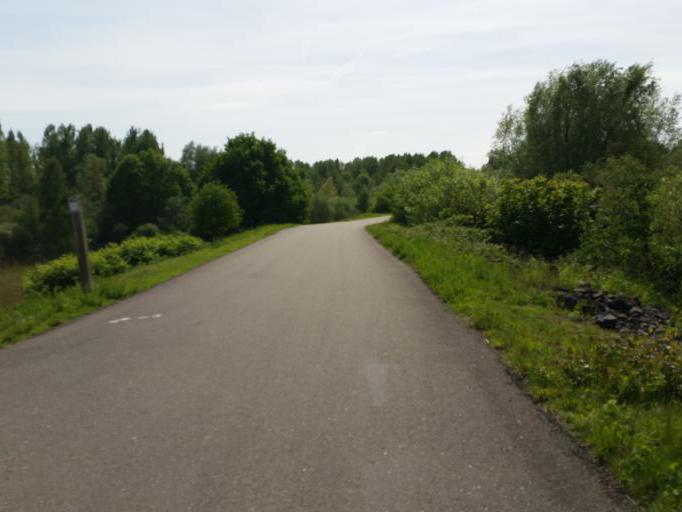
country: BE
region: Flanders
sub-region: Provincie Antwerpen
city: Boom
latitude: 51.0805
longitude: 4.3757
